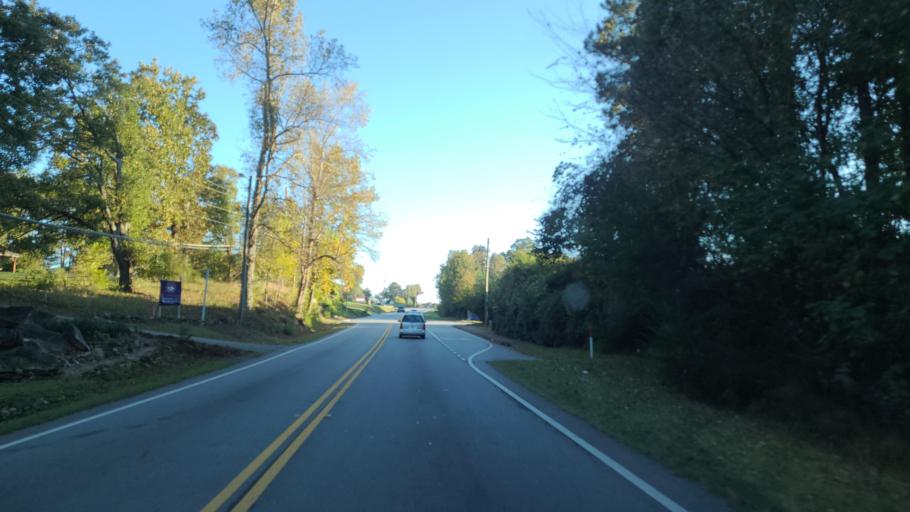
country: US
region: Georgia
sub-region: Clayton County
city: Lake City
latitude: 33.5875
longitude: -84.2929
